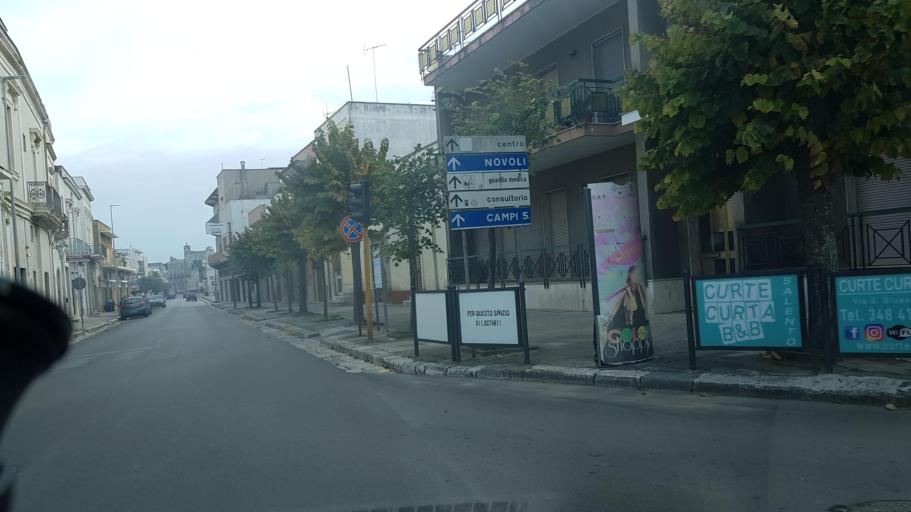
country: IT
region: Apulia
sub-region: Provincia di Lecce
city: Trepuzzi
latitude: 40.4065
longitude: 18.0697
